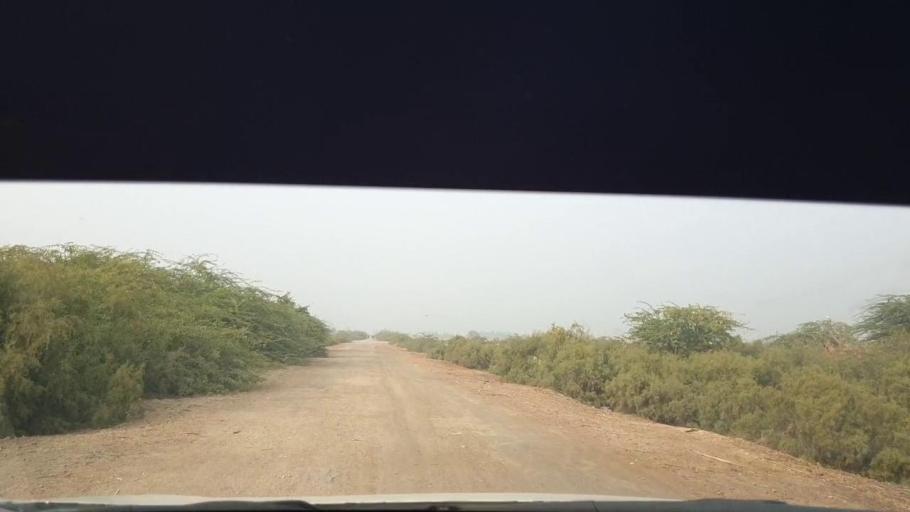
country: PK
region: Sindh
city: Berani
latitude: 25.8073
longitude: 68.8822
